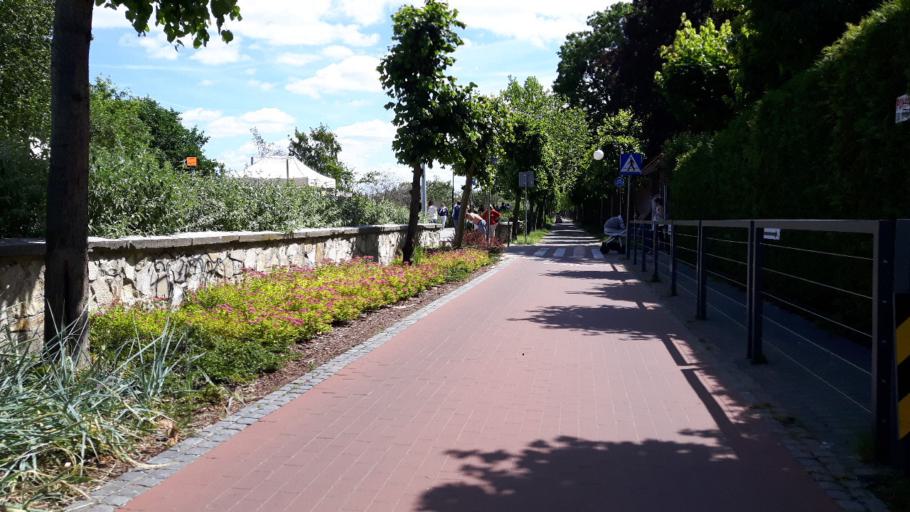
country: PL
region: Pomeranian Voivodeship
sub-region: Sopot
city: Sopot
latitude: 54.4422
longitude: 18.5743
